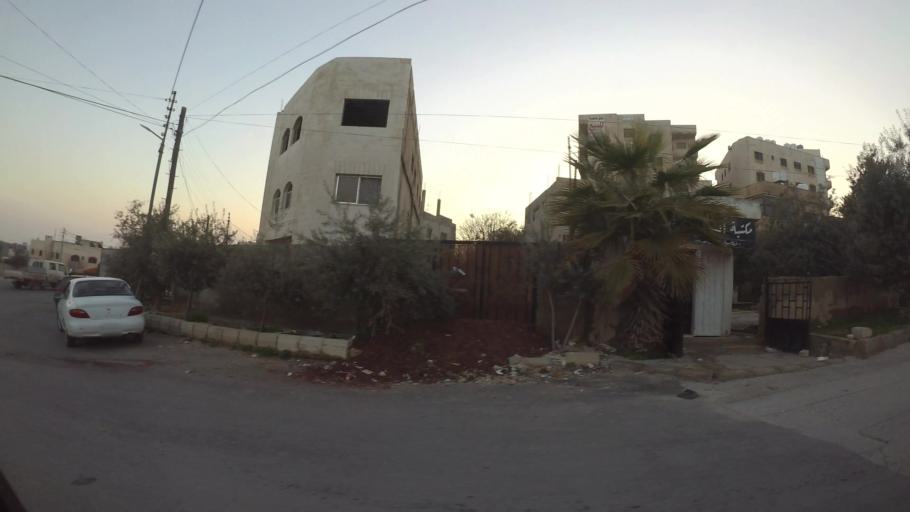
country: JO
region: Amman
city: Al Quwaysimah
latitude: 31.8962
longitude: 35.9294
